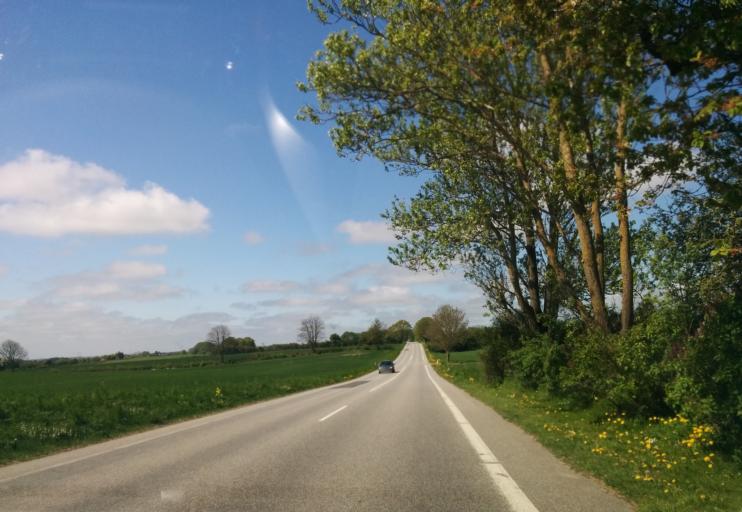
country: DK
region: South Denmark
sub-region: Assens Kommune
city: Tommerup
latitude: 55.3230
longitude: 10.2336
